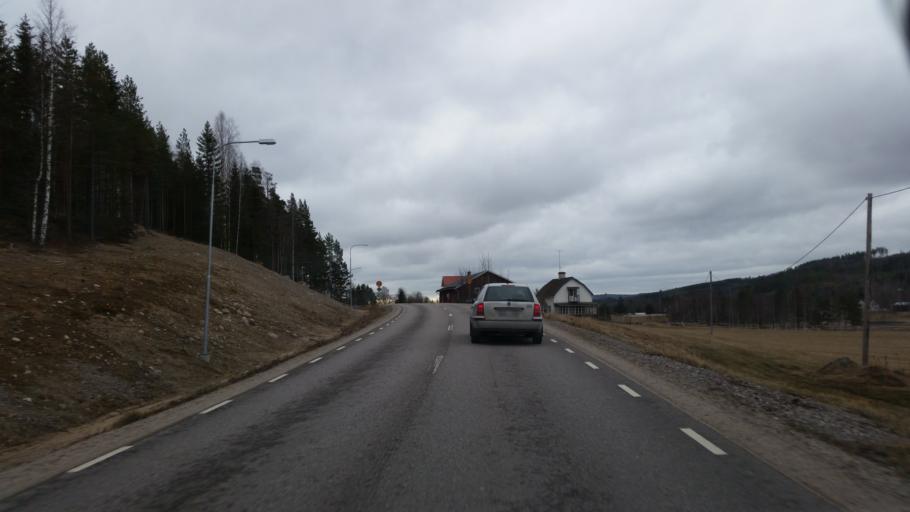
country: SE
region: Gaevleborg
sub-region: Ovanakers Kommun
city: Edsbyn
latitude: 61.4059
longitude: 15.7743
